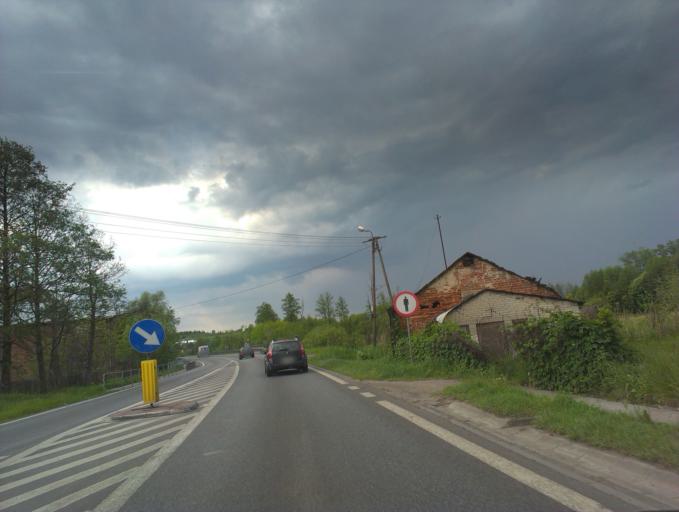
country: PL
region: Masovian Voivodeship
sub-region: Powiat grojecki
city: Pniewy
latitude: 51.8963
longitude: 20.7818
